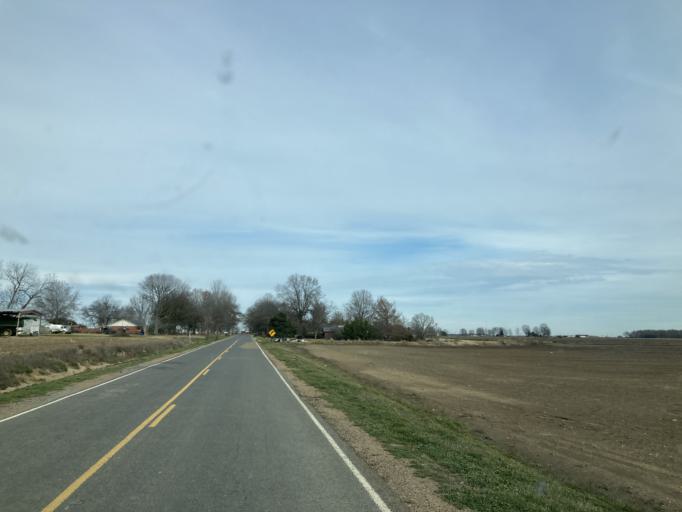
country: US
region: Mississippi
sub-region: Humphreys County
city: Belzoni
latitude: 33.1288
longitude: -90.6112
